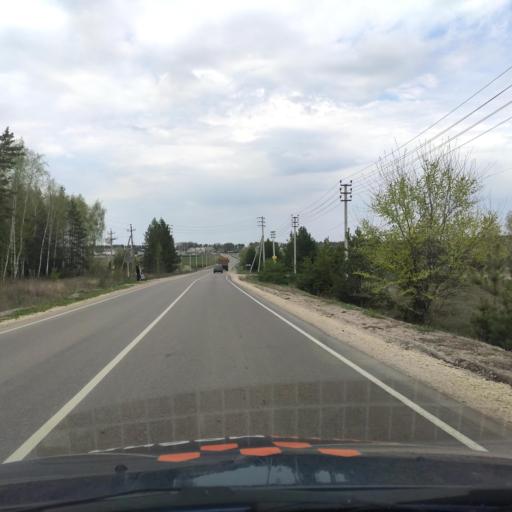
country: RU
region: Voronezj
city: Podgornoye
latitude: 51.8661
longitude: 39.1709
